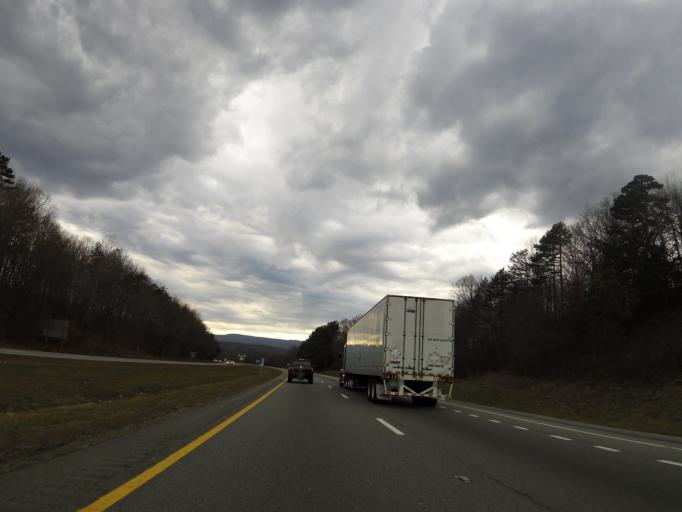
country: US
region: Tennessee
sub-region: Roane County
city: Rockwood
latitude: 35.8983
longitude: -84.7059
